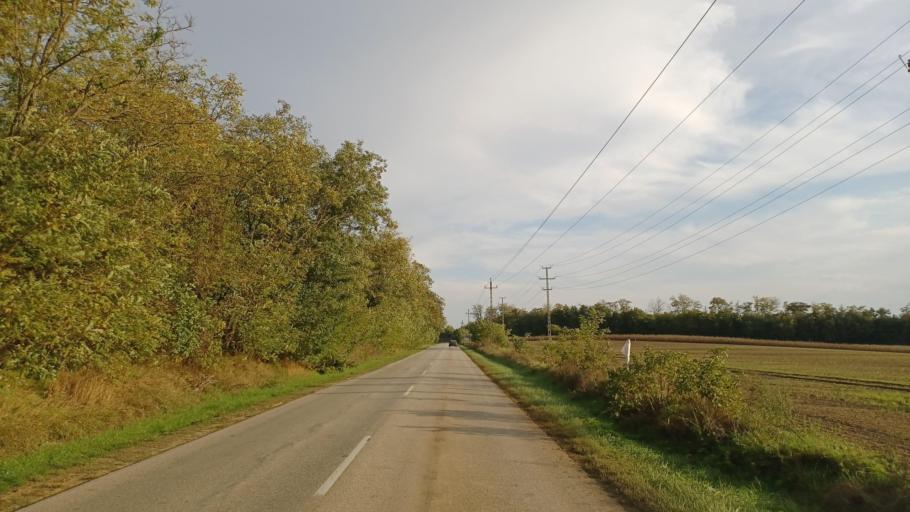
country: HU
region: Fejer
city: Baracs
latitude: 46.8396
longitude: 18.8959
